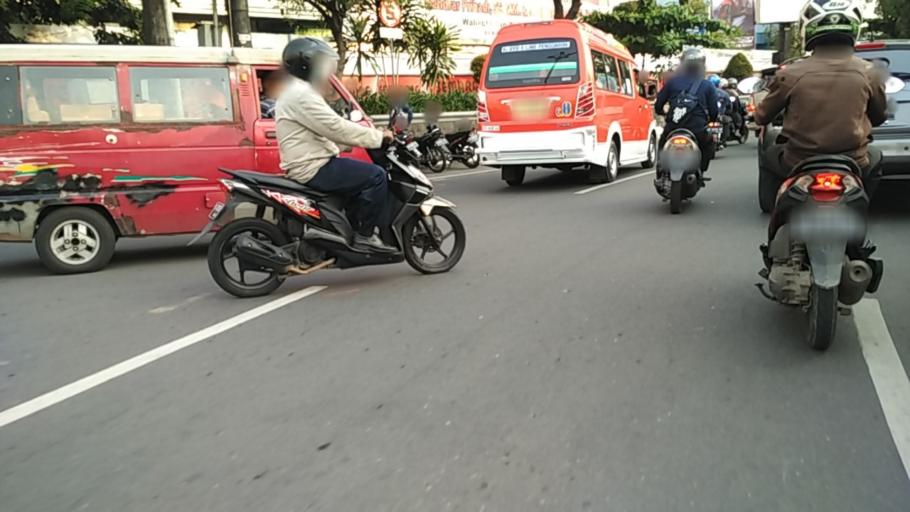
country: ID
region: Central Java
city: Semarang
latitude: -6.9898
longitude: 110.4240
